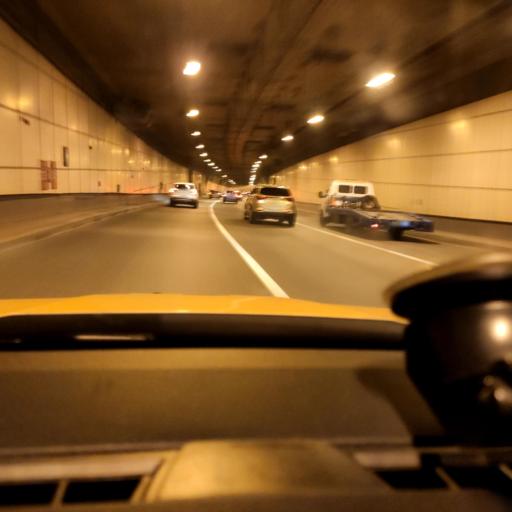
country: RU
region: Moscow
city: Strogino
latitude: 55.7730
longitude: 37.4066
